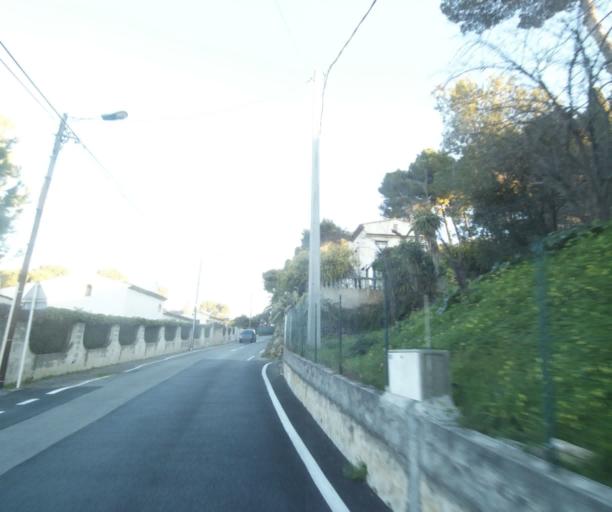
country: FR
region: Provence-Alpes-Cote d'Azur
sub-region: Departement des Alpes-Maritimes
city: Vallauris
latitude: 43.5824
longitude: 7.0812
